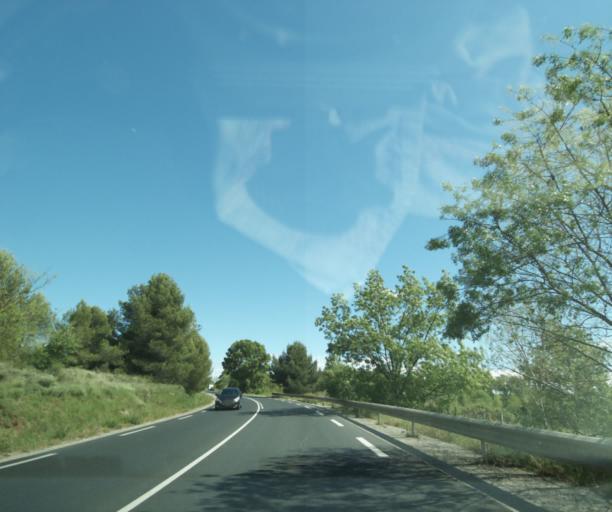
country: FR
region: Languedoc-Roussillon
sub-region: Departement de l'Herault
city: Saint-Jean-de-Vedas
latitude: 43.5895
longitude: 3.8215
